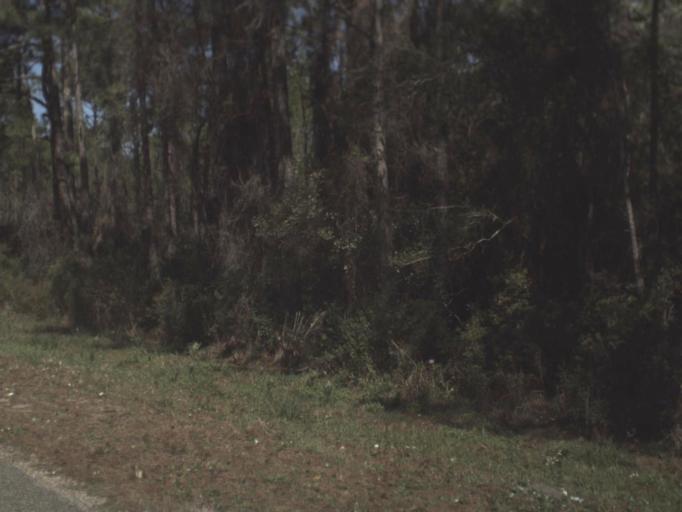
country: US
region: Florida
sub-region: Gulf County
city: Port Saint Joe
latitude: 29.7536
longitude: -85.2501
